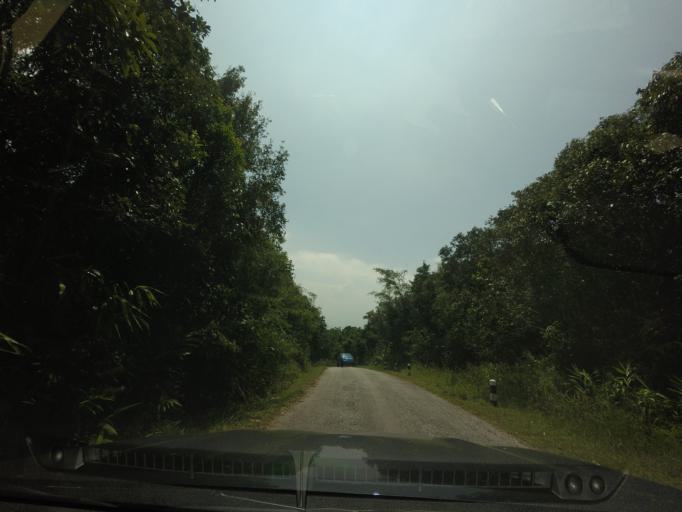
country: TH
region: Loei
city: Phu Ruea
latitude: 17.4939
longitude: 101.3508
